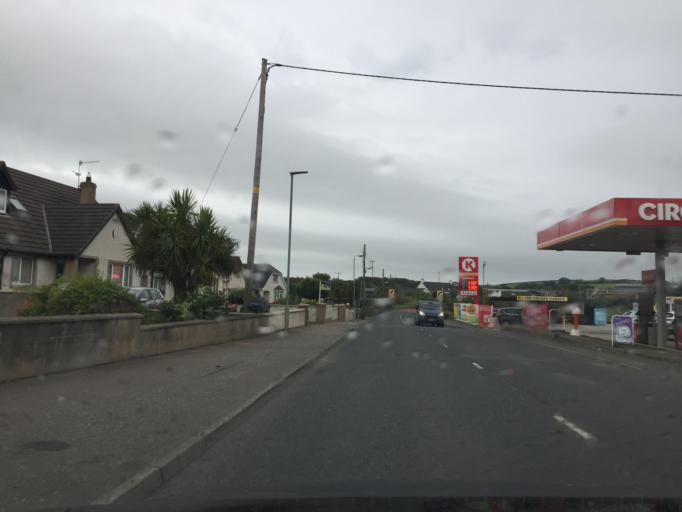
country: GB
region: Northern Ireland
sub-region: Down District
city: Kircubbin
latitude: 54.4862
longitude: -5.5305
